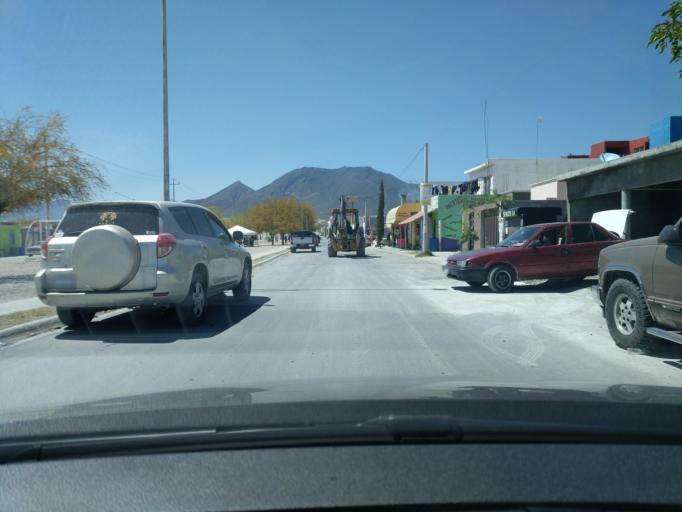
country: MX
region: Nuevo Leon
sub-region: Salinas Victoria
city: Las Torres
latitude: 25.9652
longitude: -100.3075
